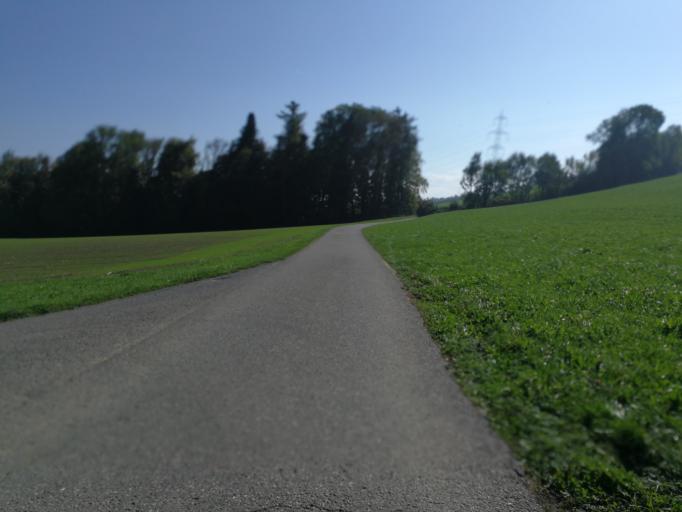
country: CH
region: Zurich
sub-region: Bezirk Uster
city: Hinteregg
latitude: 47.3151
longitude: 8.6853
